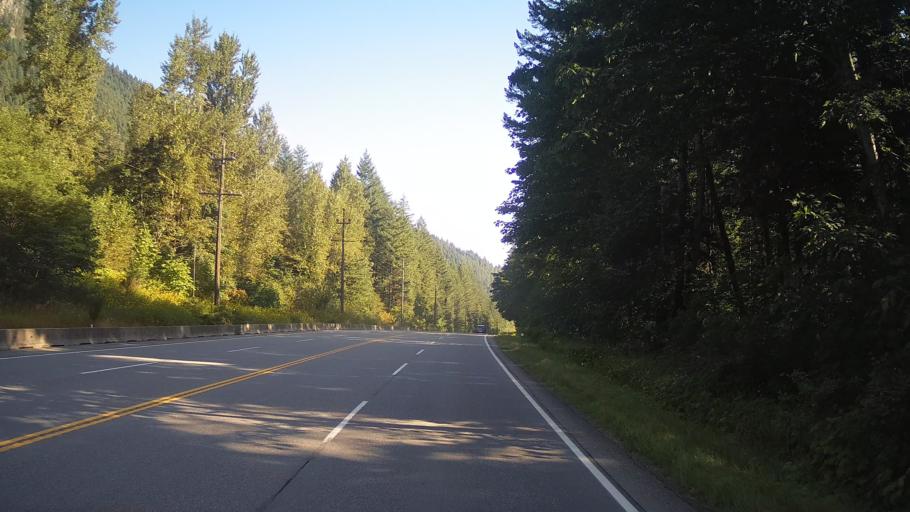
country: CA
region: British Columbia
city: Hope
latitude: 49.4494
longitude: -121.4374
